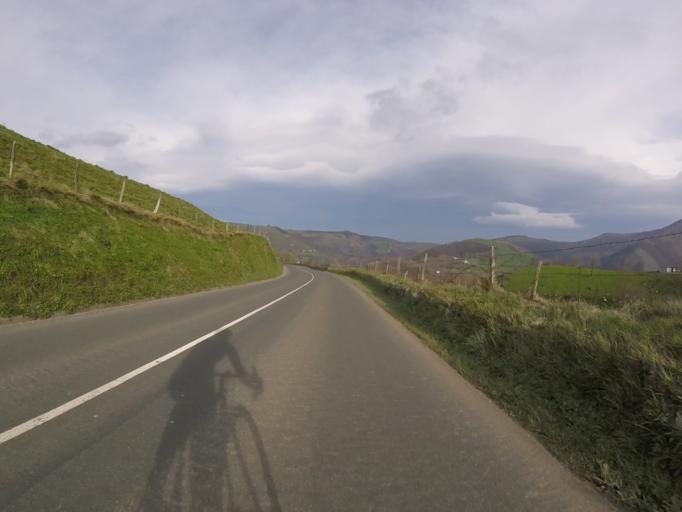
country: ES
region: Basque Country
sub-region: Provincia de Guipuzcoa
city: Beizama
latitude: 43.1666
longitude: -2.2218
